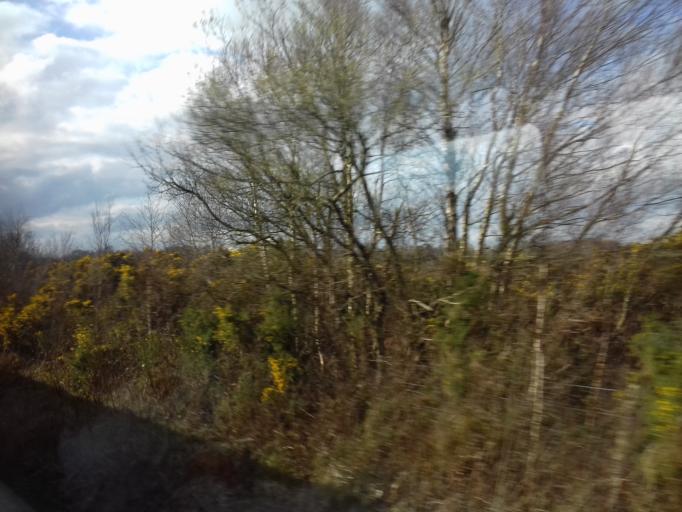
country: IE
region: Leinster
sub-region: An Iarmhi
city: Kinnegad
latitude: 53.4768
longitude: -7.0476
